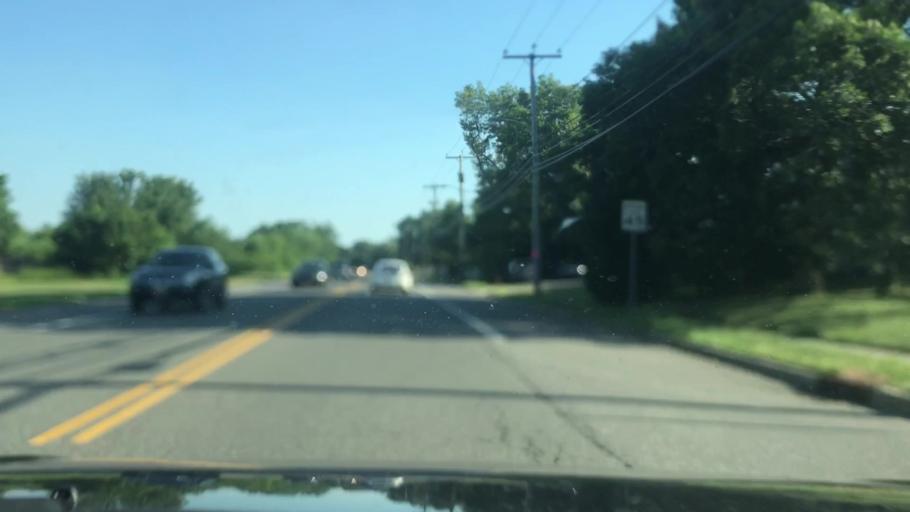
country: US
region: New Jersey
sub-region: Ocean County
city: Leisure Village
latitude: 40.0105
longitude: -74.2024
